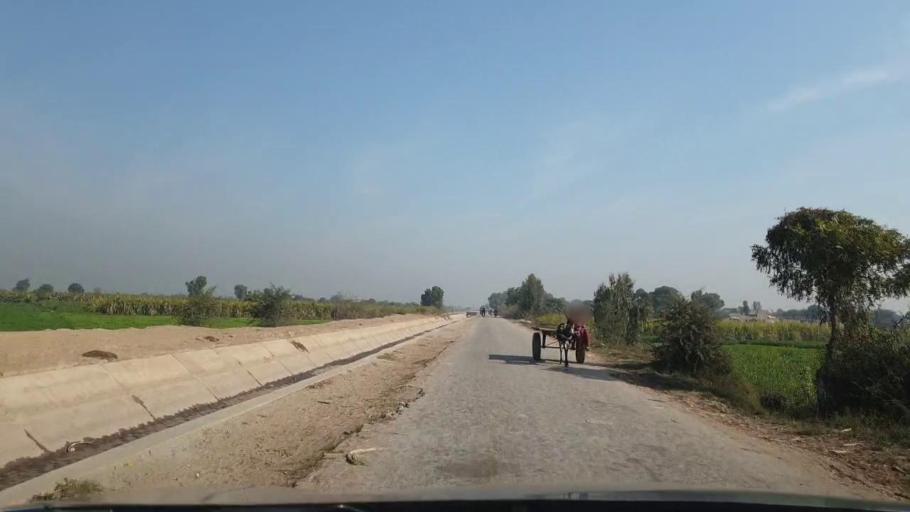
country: PK
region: Sindh
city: Tando Allahyar
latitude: 25.5908
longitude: 68.7166
